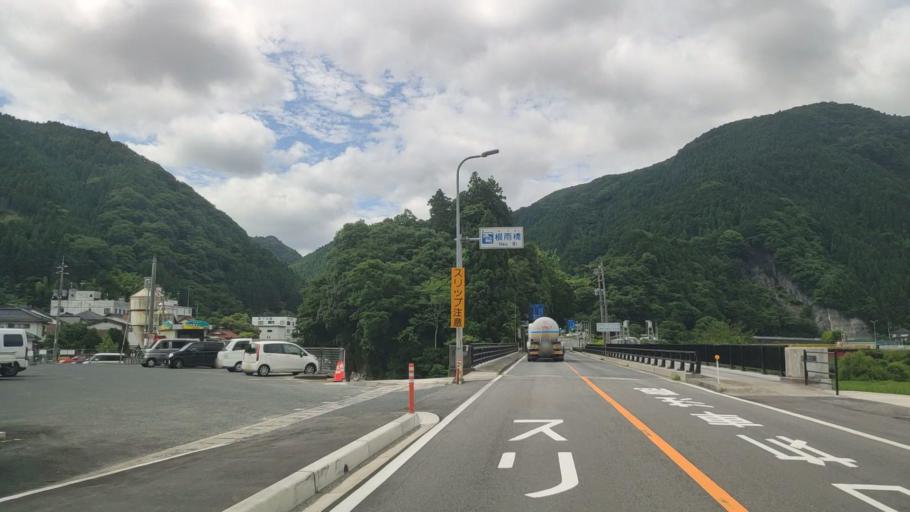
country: JP
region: Tottori
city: Yonago
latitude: 35.2389
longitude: 133.4401
